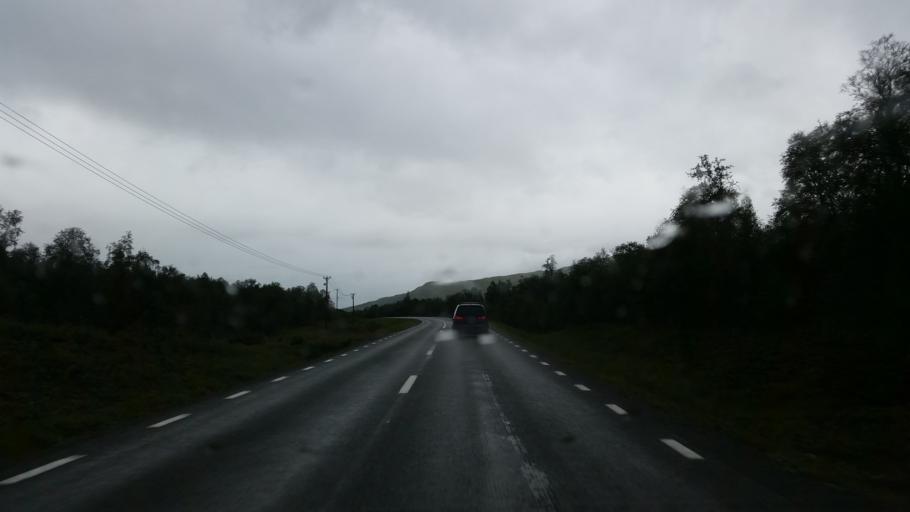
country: NO
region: Nordland
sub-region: Rana
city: Mo i Rana
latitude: 65.9117
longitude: 14.9908
